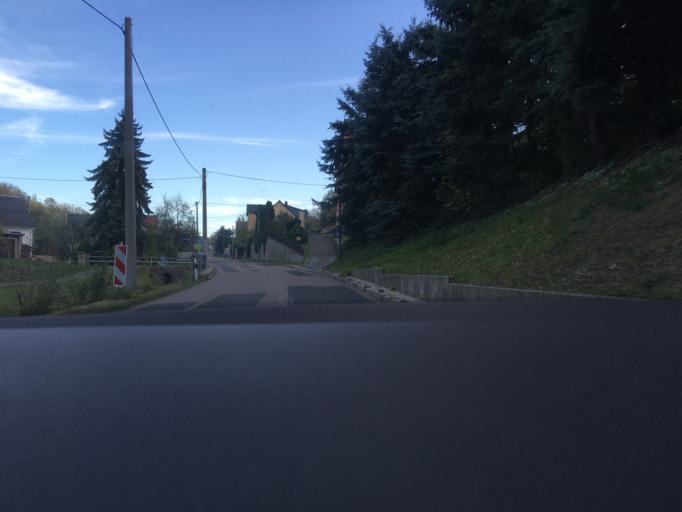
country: DE
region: Saxony
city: Glashutte
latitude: 50.8401
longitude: 13.7995
